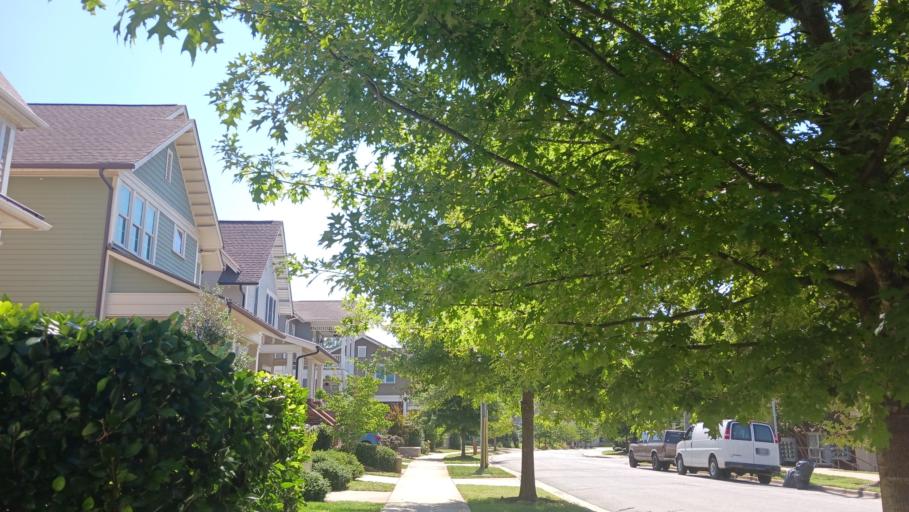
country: US
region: North Carolina
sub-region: Mecklenburg County
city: Charlotte
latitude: 35.2088
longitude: -80.8313
